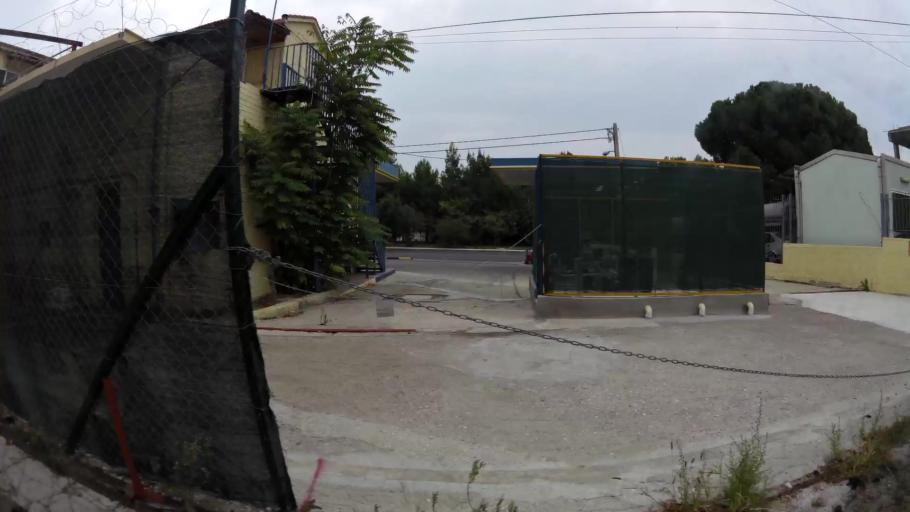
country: GR
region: Attica
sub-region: Nomarchia Athinas
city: Agioi Anargyroi
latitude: 38.0349
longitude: 23.7162
